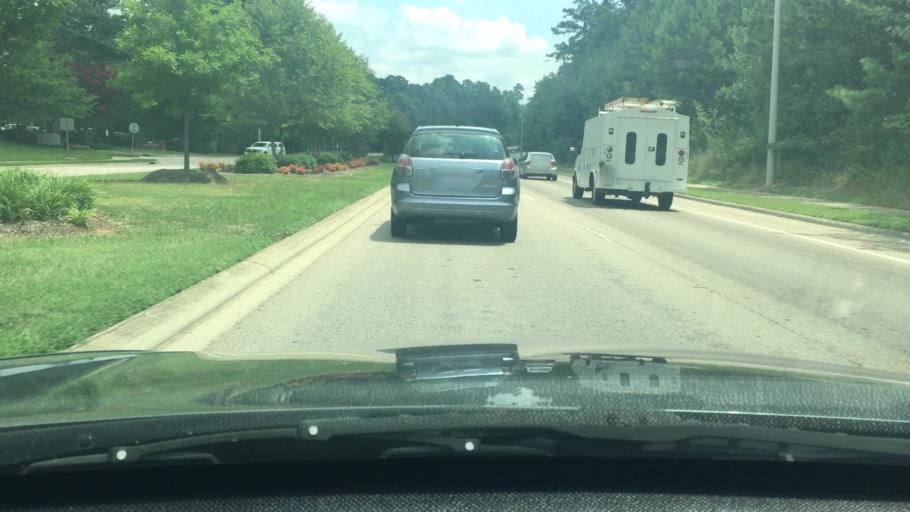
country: US
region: North Carolina
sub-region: Wake County
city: Cary
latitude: 35.7957
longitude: -78.7613
